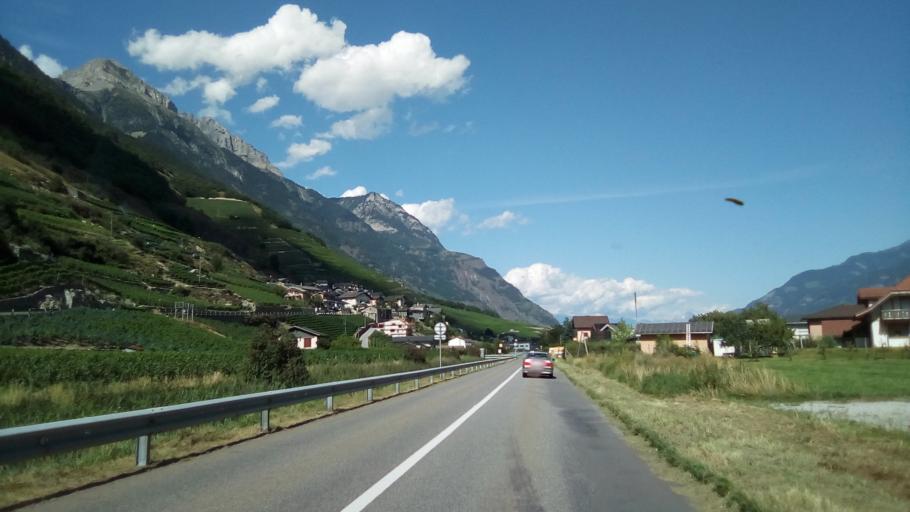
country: CH
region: Valais
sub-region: Martigny District
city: Martigny-Ville
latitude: 46.1257
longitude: 7.0872
